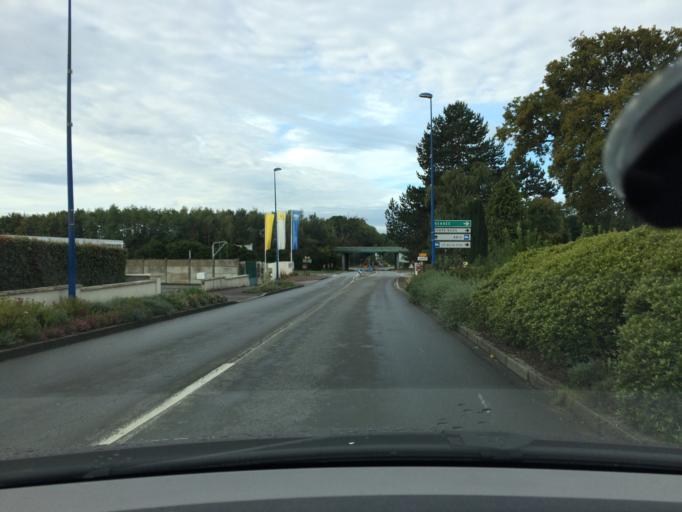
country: FR
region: Brittany
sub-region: Departement d'Ille-et-Vilaine
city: Janze
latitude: 47.9529
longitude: -1.5067
